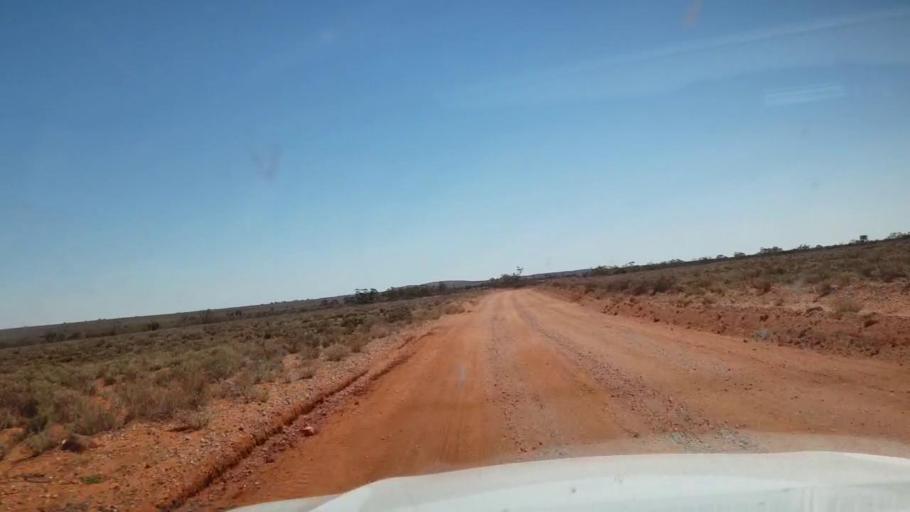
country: AU
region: South Australia
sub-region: Whyalla
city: Whyalla
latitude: -32.6859
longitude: 137.1124
